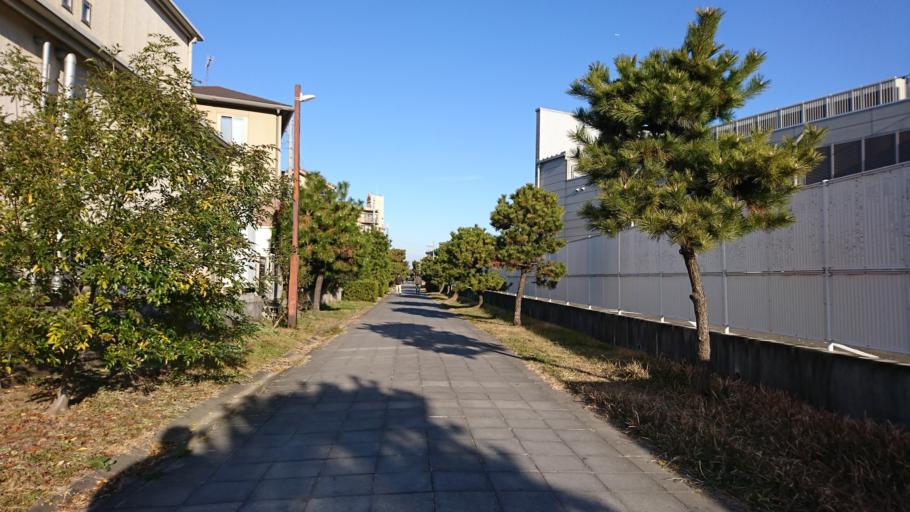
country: JP
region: Hyogo
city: Kakogawacho-honmachi
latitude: 34.7360
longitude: 134.8486
